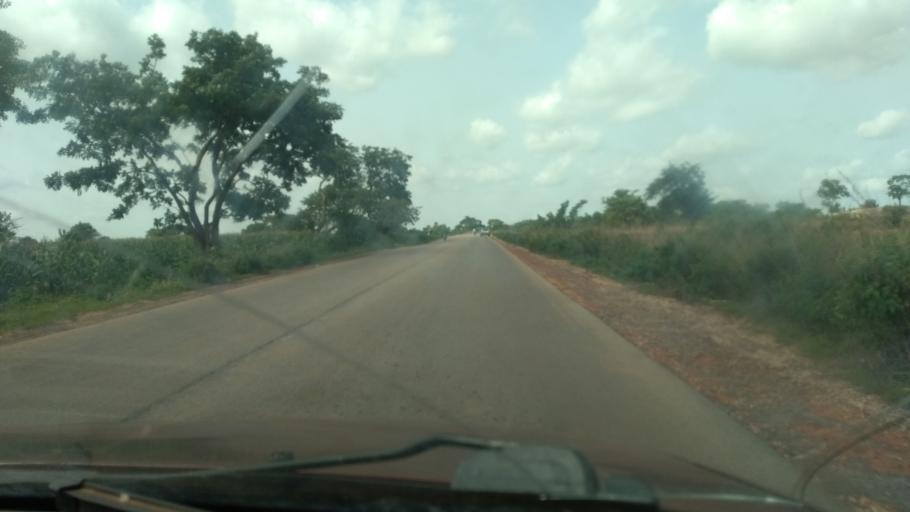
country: NG
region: Katsina
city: Sabuwa
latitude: 11.0523
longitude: 7.1623
